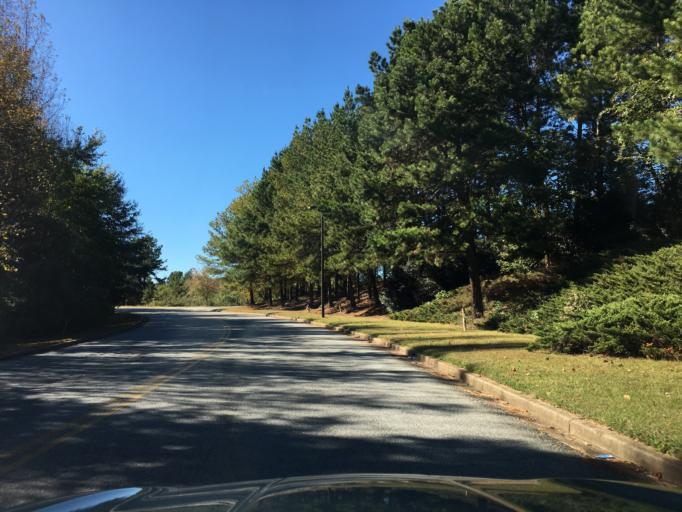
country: US
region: South Carolina
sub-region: Spartanburg County
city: Wellford
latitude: 34.9163
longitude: -82.1015
